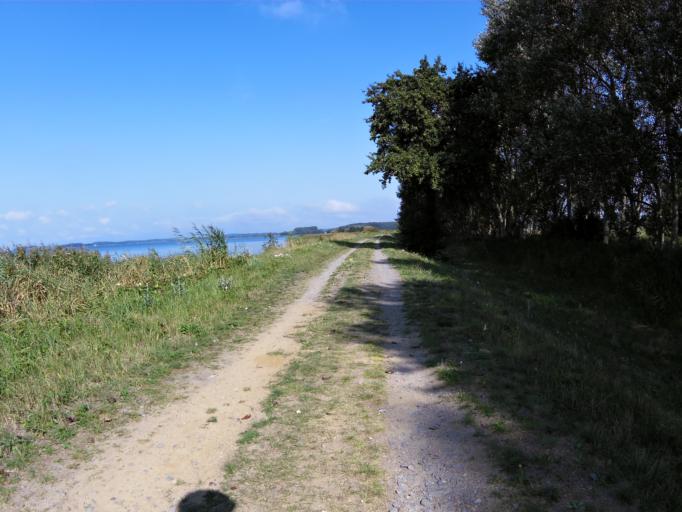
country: DE
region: Mecklenburg-Vorpommern
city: Loddin
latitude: 53.9833
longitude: 14.0484
